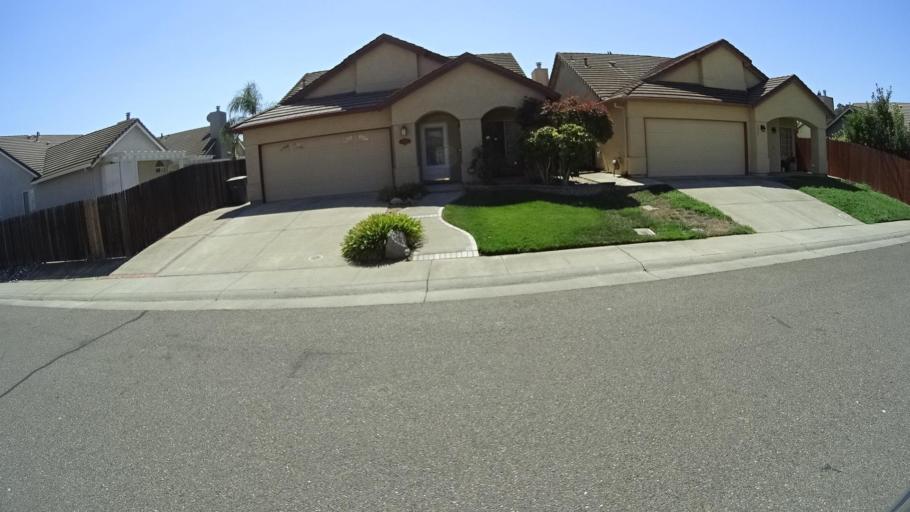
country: US
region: California
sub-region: Sacramento County
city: Laguna
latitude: 38.4182
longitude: -121.4097
